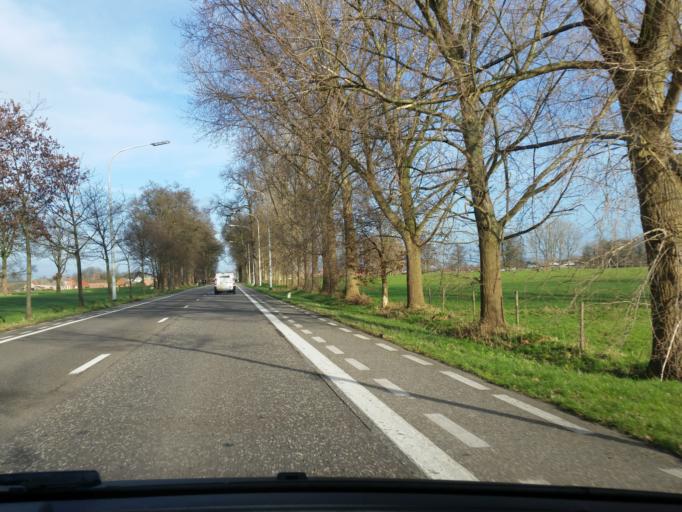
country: BE
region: Flanders
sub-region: Provincie Antwerpen
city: Wuustwezel
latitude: 51.4003
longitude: 4.6043
